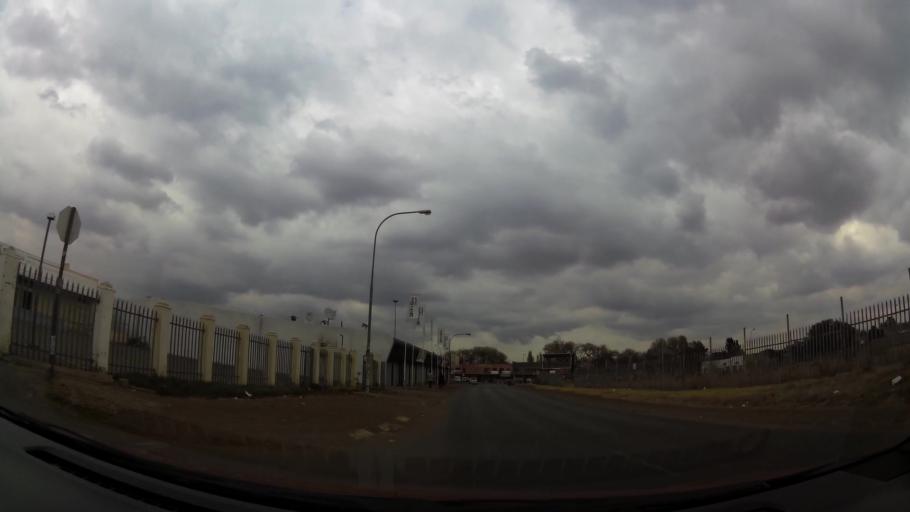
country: ZA
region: Gauteng
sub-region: City of Johannesburg Metropolitan Municipality
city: Soweto
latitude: -26.2605
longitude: 27.8473
